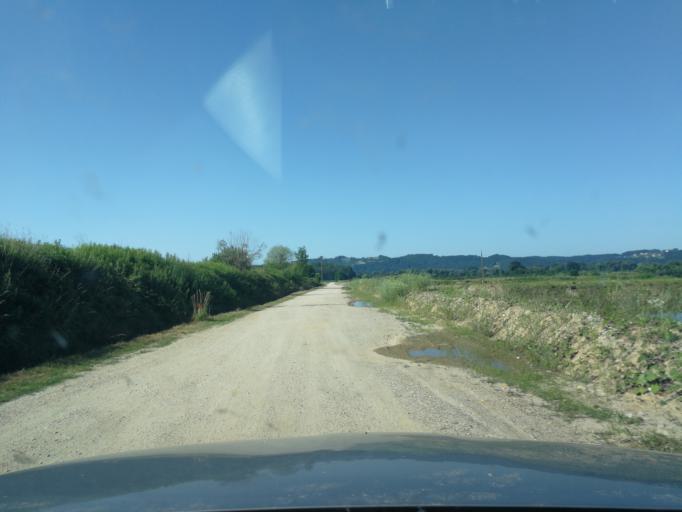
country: AT
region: Burgenland
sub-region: Politischer Bezirk Jennersdorf
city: Konigsdorf
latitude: 47.0146
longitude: 16.1611
